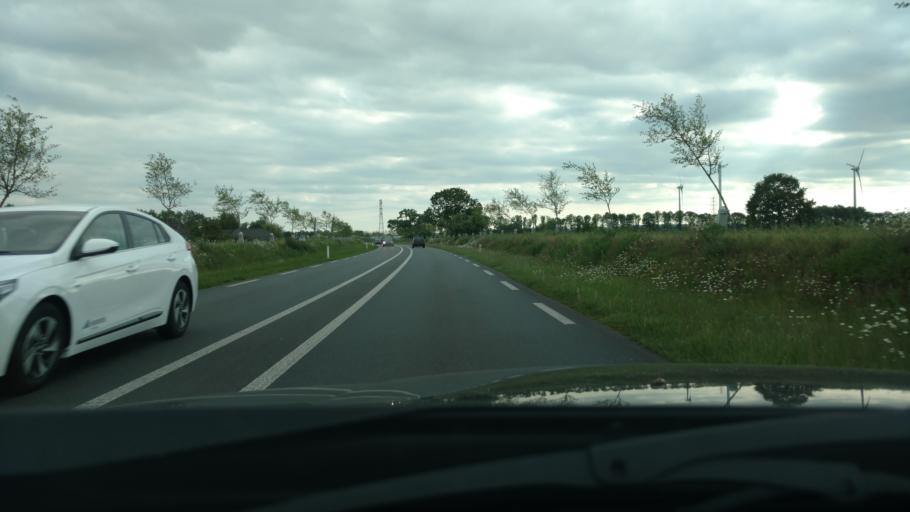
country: NL
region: Gelderland
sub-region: Gemeente Lochem
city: Eefde
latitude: 52.1661
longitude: 6.2067
